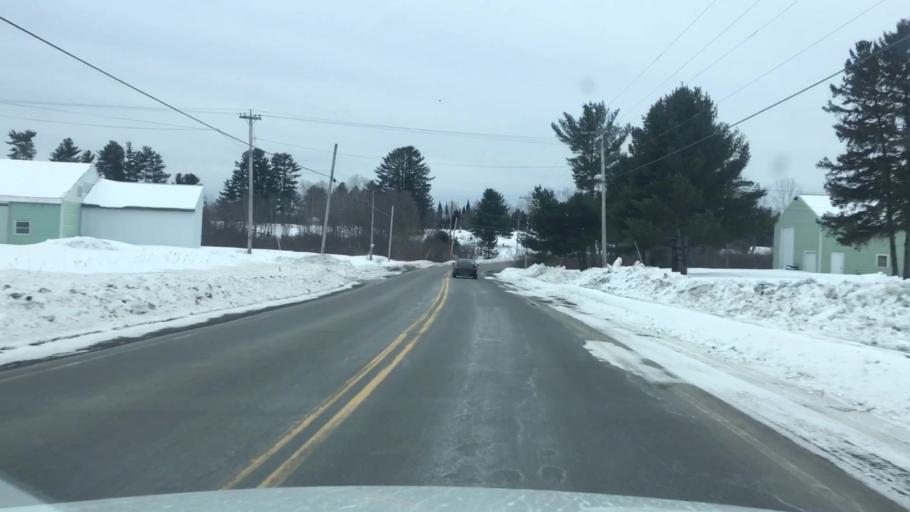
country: US
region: Maine
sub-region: Penobscot County
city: Charleston
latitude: 44.9983
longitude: -69.0361
